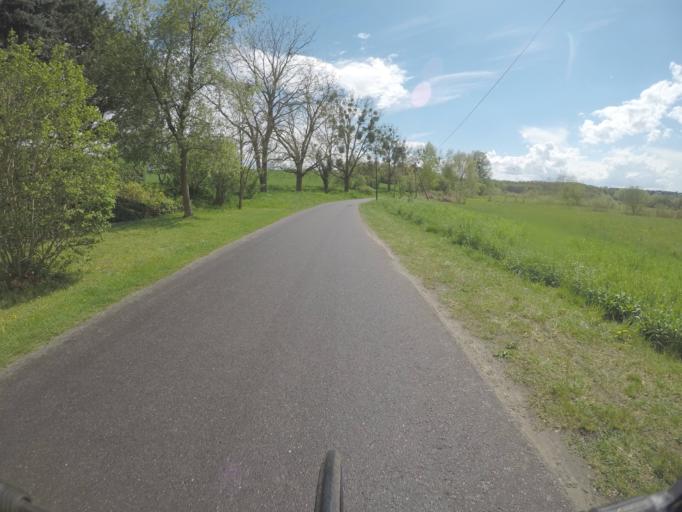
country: DE
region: Brandenburg
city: Biesenthal
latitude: 52.7617
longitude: 13.6308
